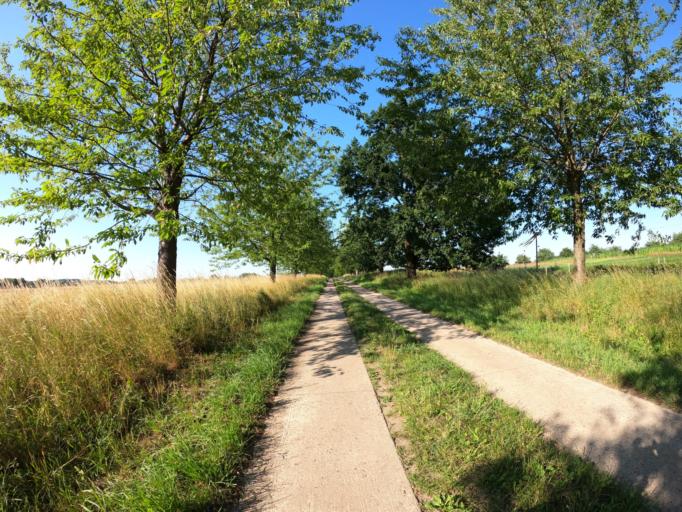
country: DE
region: Brandenburg
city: Tantow
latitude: 53.2405
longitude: 14.3683
